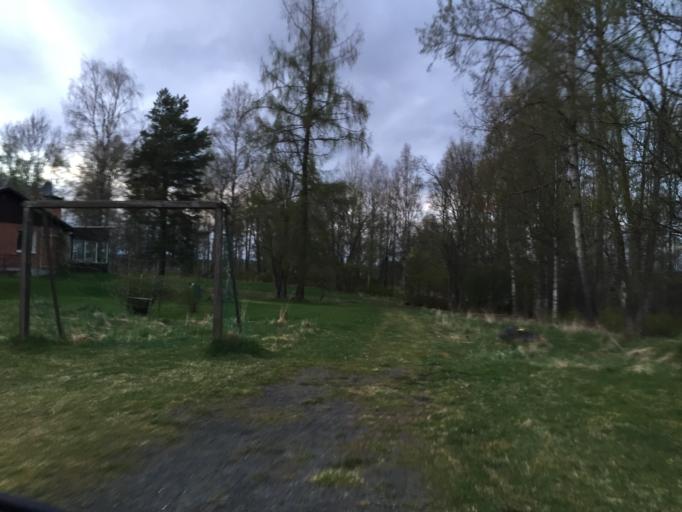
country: SE
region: Dalarna
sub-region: Ludvika Kommun
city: Ludvika
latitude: 60.1404
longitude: 15.2044
